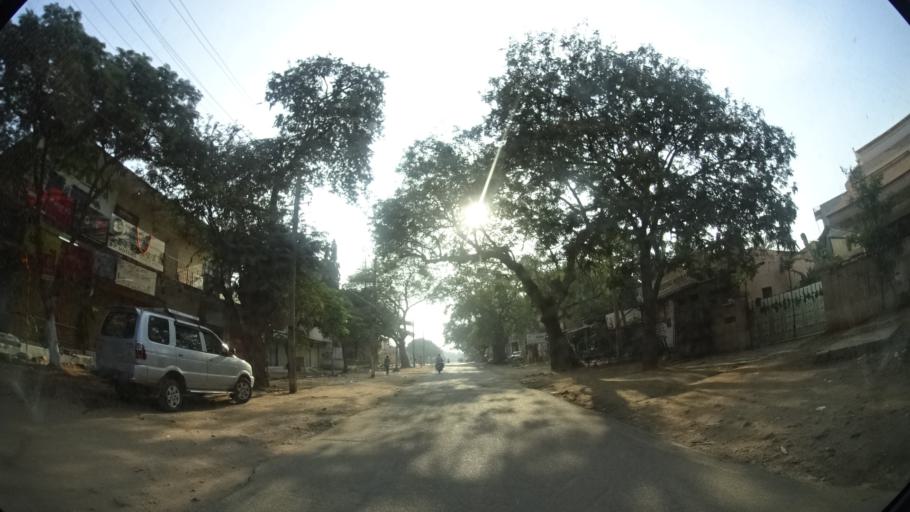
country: IN
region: Karnataka
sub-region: Bellary
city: Hospet
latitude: 15.2658
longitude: 76.4002
